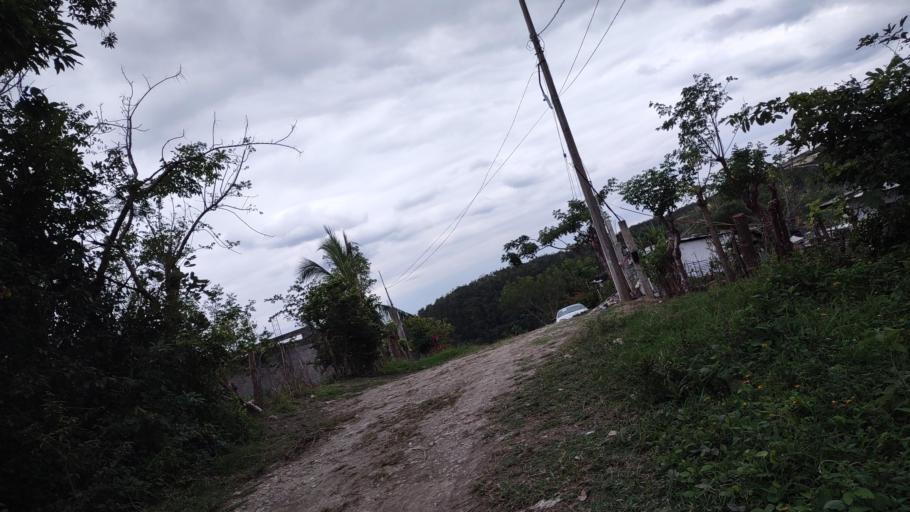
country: MX
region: Veracruz
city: Papantla de Olarte
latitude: 20.4317
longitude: -97.3397
